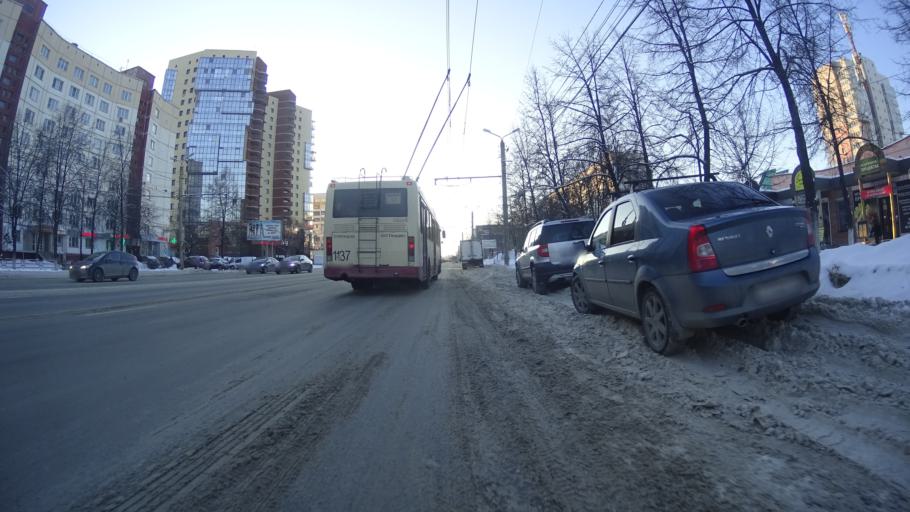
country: RU
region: Chelyabinsk
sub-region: Gorod Chelyabinsk
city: Chelyabinsk
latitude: 55.1946
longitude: 61.3439
